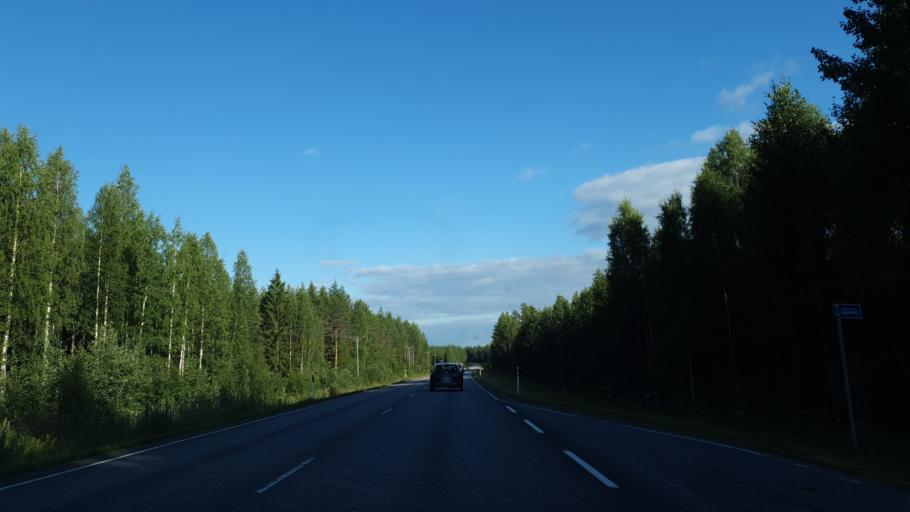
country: FI
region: North Karelia
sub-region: Joensuu
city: Outokumpu
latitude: 62.5288
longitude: 28.9883
